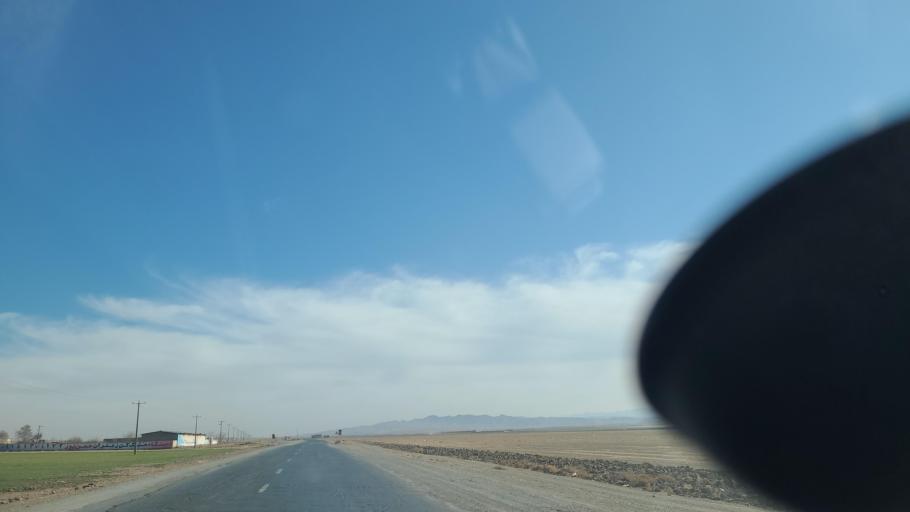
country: IR
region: Razavi Khorasan
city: Dowlatabad
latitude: 35.5998
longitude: 59.4683
